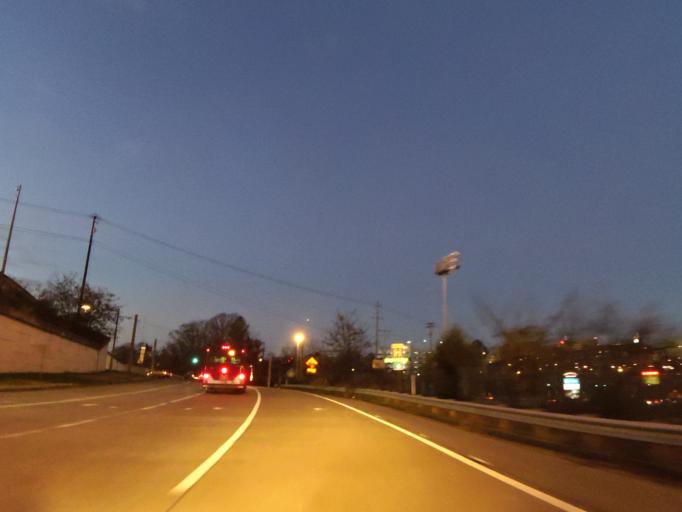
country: US
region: Tennessee
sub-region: Knox County
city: Knoxville
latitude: 35.9518
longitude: -83.9419
